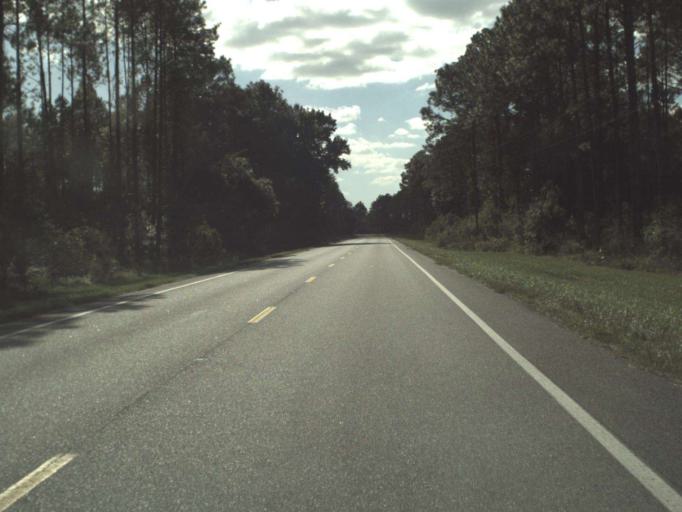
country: US
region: Florida
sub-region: Leon County
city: Woodville
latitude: 30.3390
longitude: -84.0187
